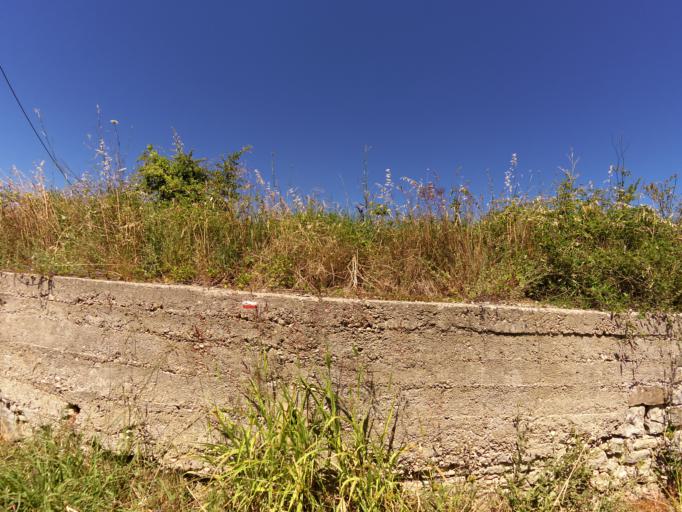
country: FR
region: Languedoc-Roussillon
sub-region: Departement du Gard
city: Boisset-et-Gaujac
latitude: 44.0236
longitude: 3.9934
